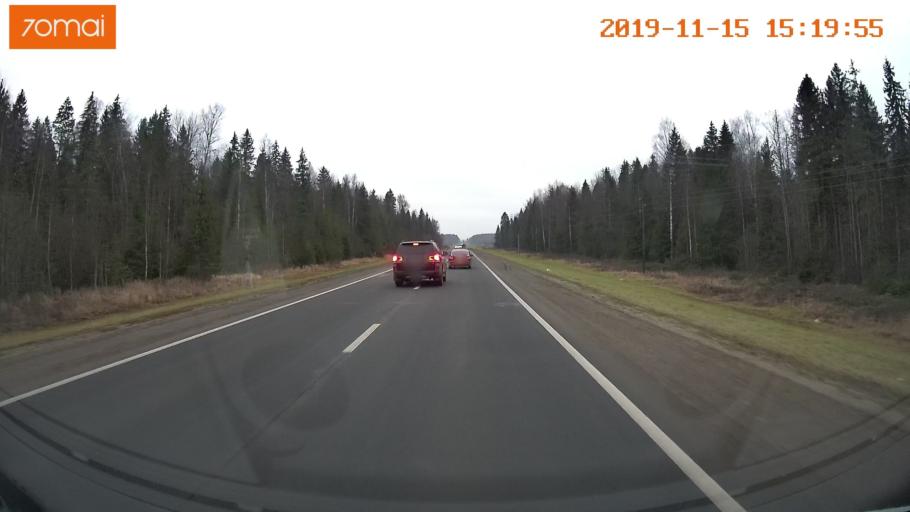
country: RU
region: Jaroslavl
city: Danilov
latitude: 58.2293
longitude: 40.1702
